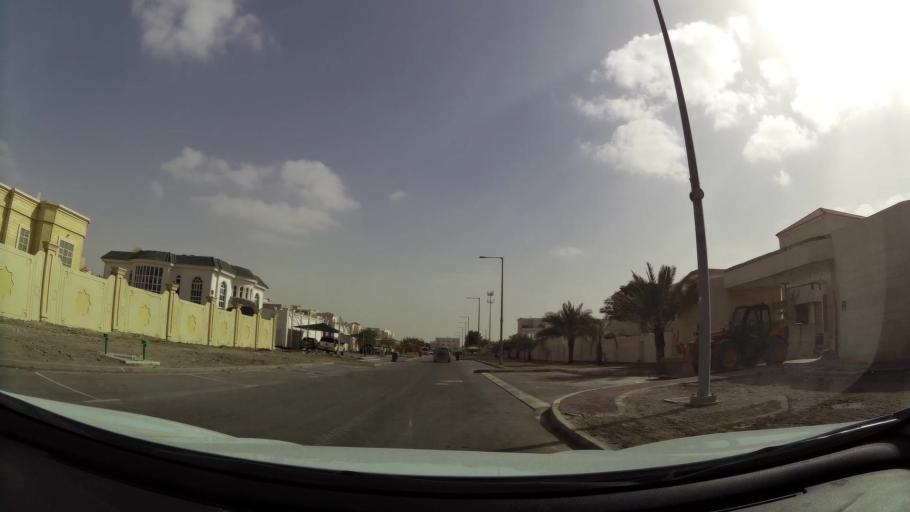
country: AE
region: Abu Dhabi
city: Abu Dhabi
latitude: 24.4204
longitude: 54.5522
